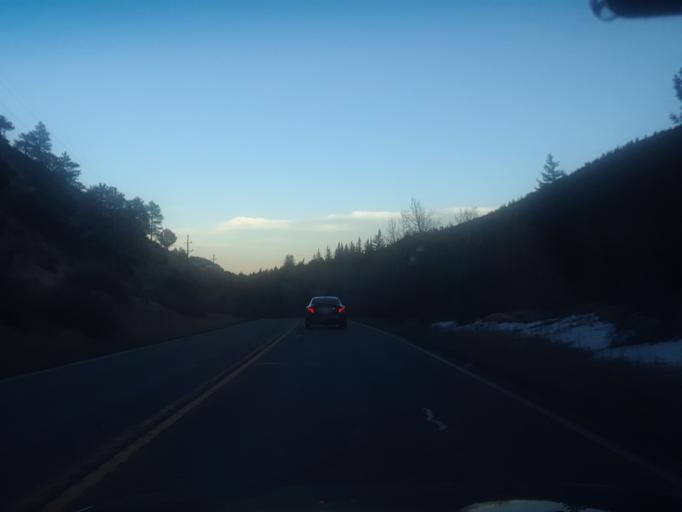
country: US
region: Colorado
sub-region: Clear Creek County
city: Georgetown
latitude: 39.4569
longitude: -105.6537
